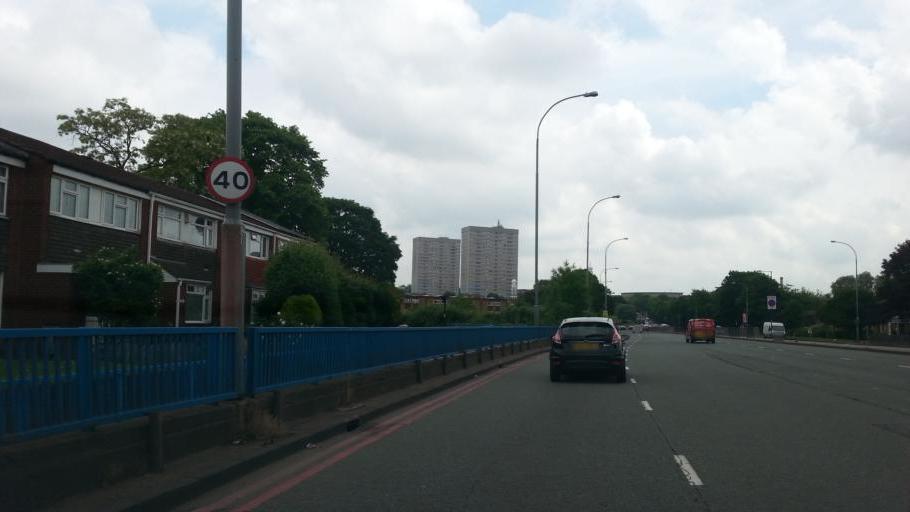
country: GB
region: England
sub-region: City and Borough of Birmingham
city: Birmingham
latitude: 52.4660
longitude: -1.8958
